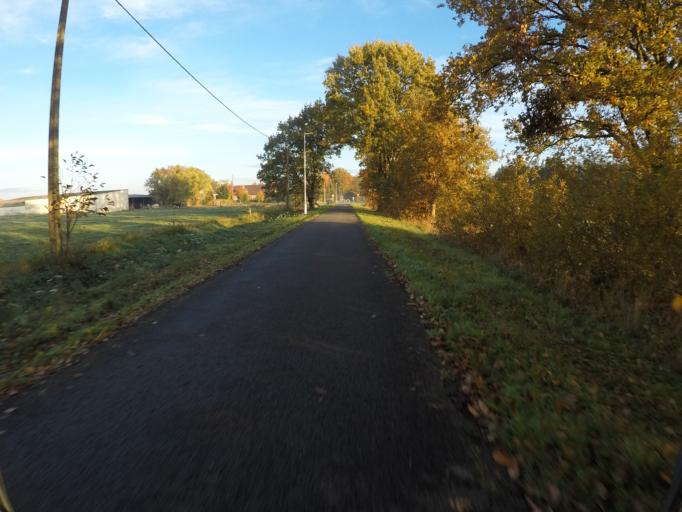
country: BE
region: Flanders
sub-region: Provincie Antwerpen
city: Olen
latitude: 51.1132
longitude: 4.8255
